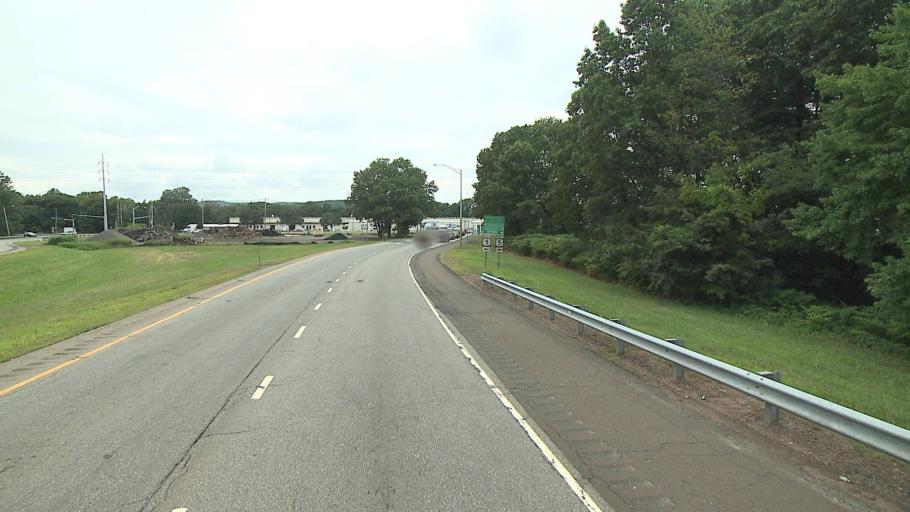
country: US
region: Connecticut
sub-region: New Haven County
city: Wallingford Center
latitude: 41.4288
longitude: -72.8350
